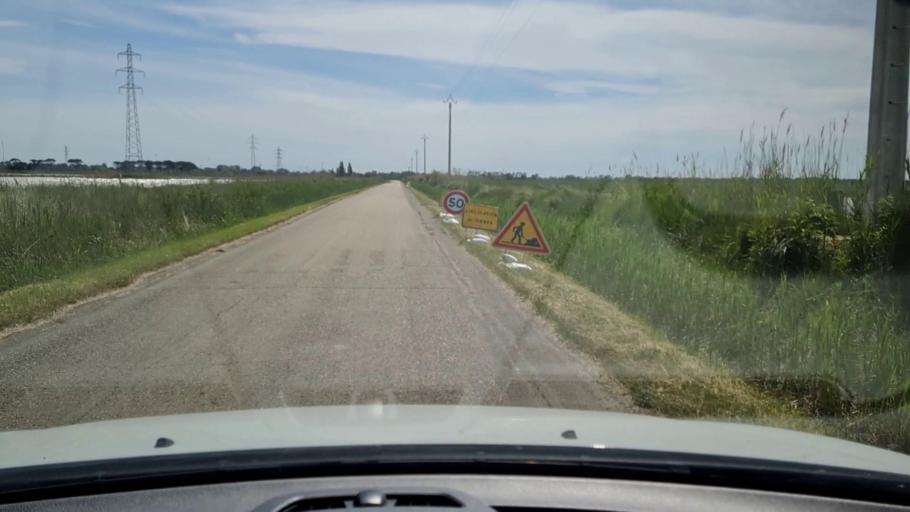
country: FR
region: Languedoc-Roussillon
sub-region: Departement du Gard
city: Saint-Gilles
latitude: 43.5788
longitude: 4.3988
